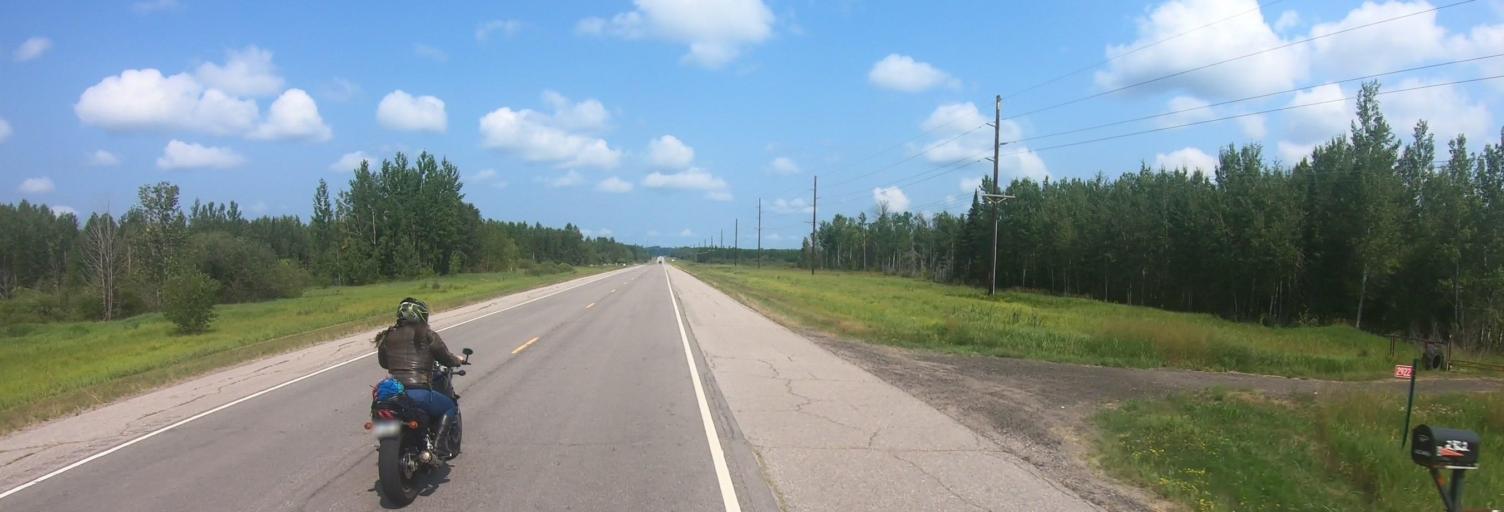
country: US
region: Minnesota
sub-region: Saint Louis County
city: Chisholm
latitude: 47.9374
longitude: -92.8286
